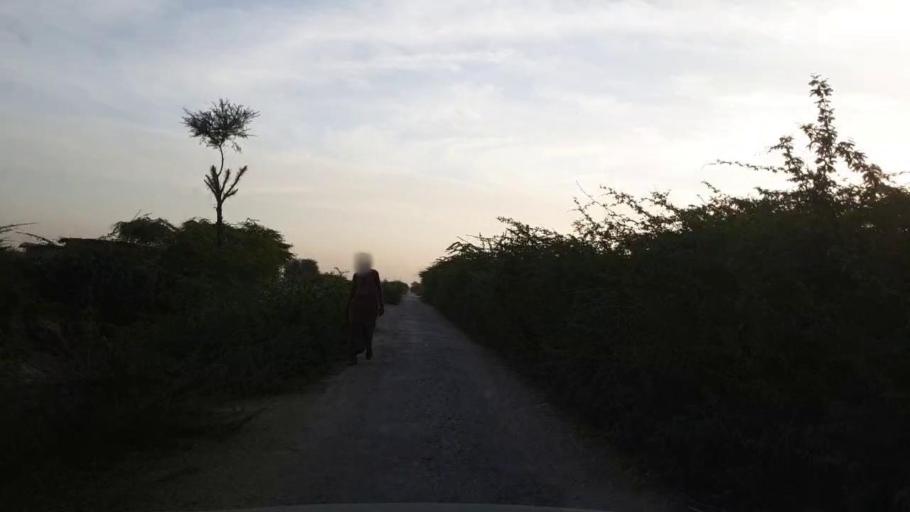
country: PK
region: Sindh
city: Kunri
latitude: 25.1174
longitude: 69.5657
